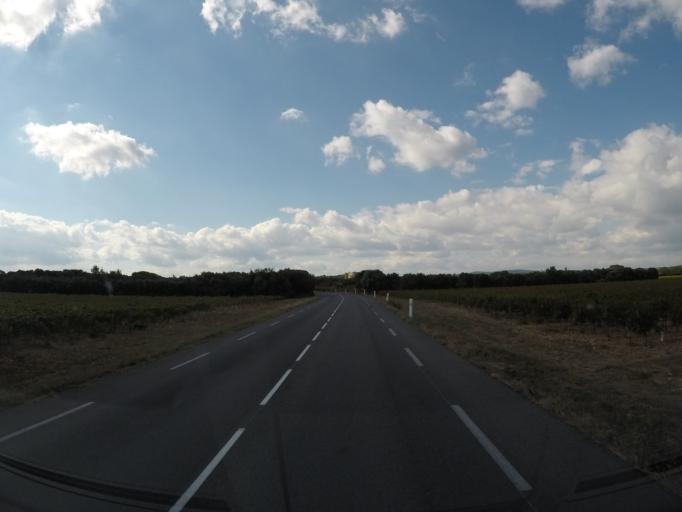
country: FR
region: Rhone-Alpes
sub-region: Departement de la Drome
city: Suze-la-Rousse
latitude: 44.2881
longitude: 4.8526
